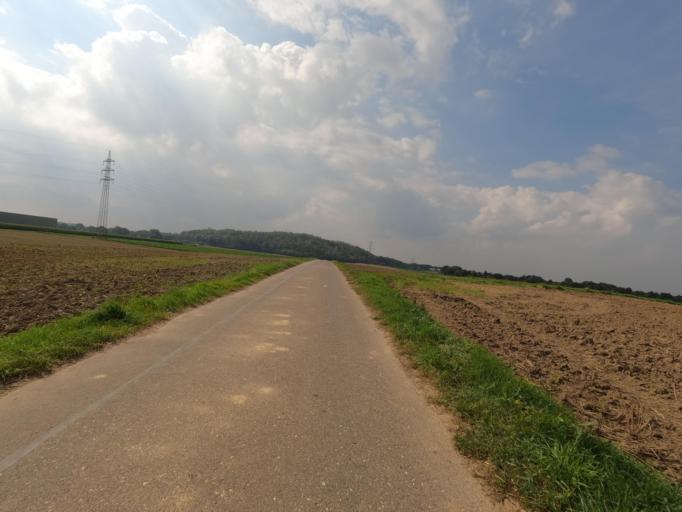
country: DE
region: North Rhine-Westphalia
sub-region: Regierungsbezirk Koln
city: Ubach-Palenberg
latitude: 50.9292
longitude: 6.1314
